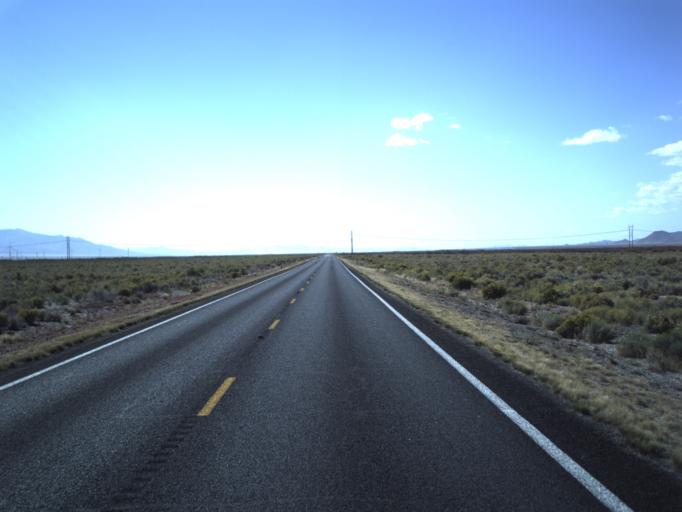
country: US
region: Utah
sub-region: Beaver County
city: Milford
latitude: 38.5822
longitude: -112.9890
